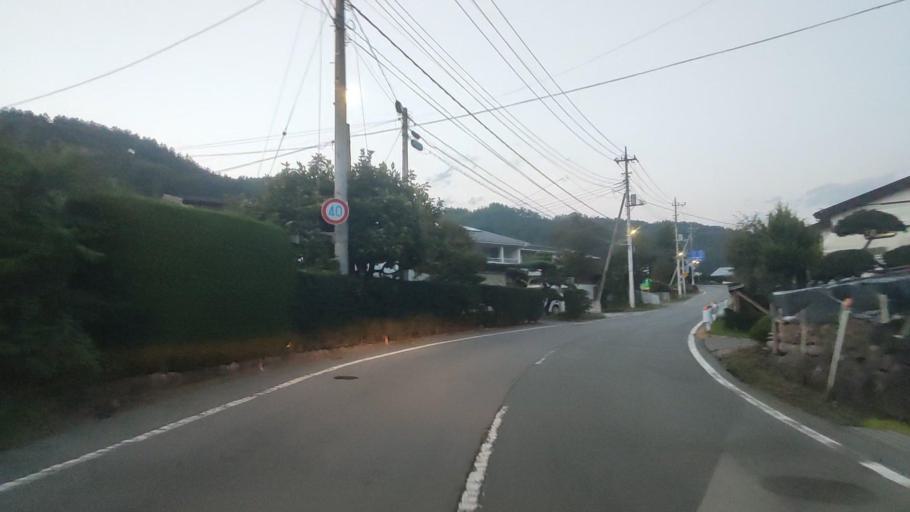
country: JP
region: Gunma
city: Nakanojomachi
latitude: 36.5477
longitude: 138.6048
